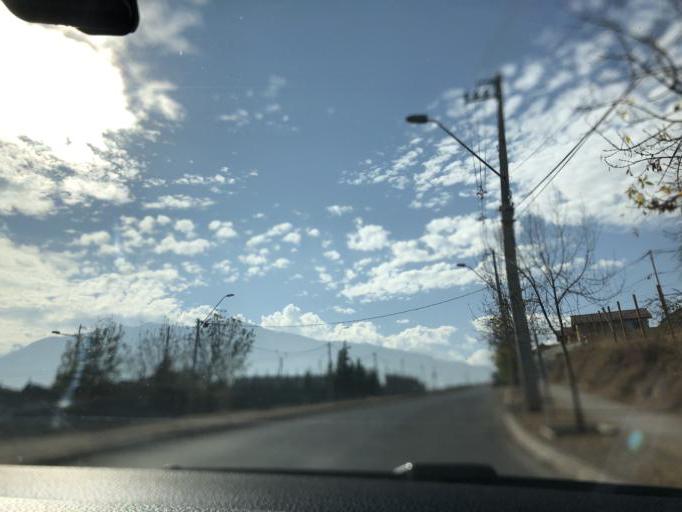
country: CL
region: Santiago Metropolitan
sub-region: Provincia de Cordillera
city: Puente Alto
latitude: -33.5877
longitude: -70.5354
